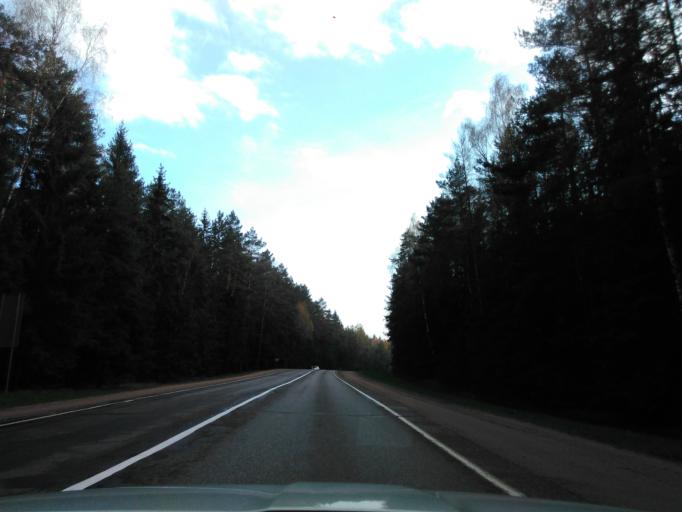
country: BY
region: Minsk
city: Lahoysk
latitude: 54.2533
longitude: 27.8521
